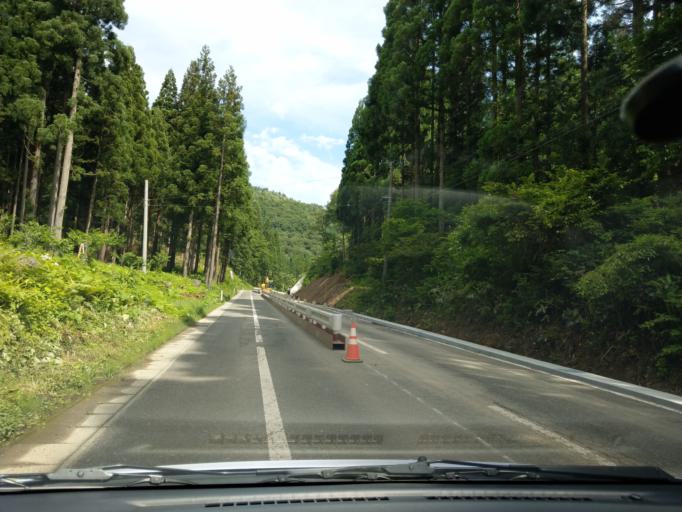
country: JP
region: Akita
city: Kakunodatemachi
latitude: 39.7213
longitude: 140.5837
